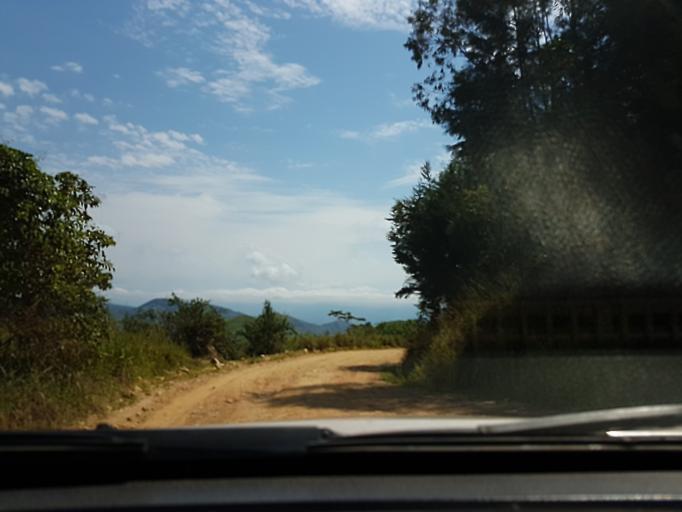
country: RW
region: Western Province
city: Cyangugu
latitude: -2.6999
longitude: 28.9089
